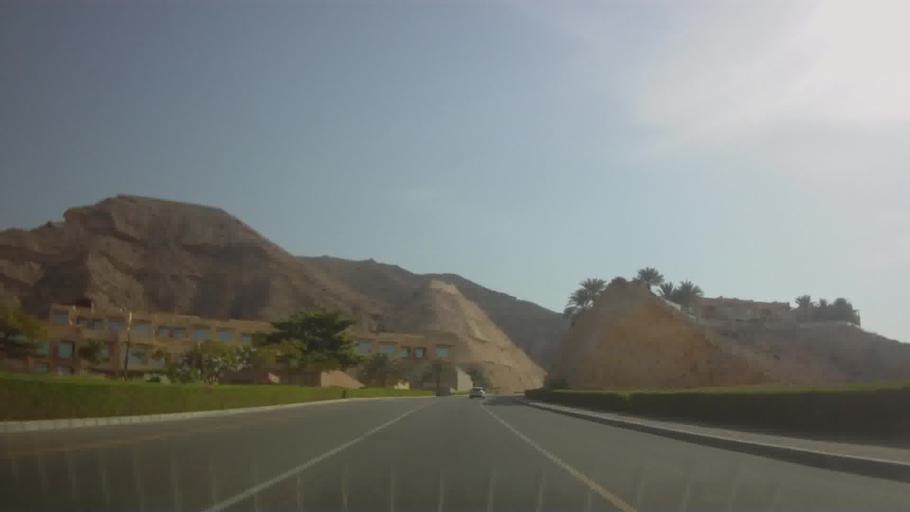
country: OM
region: Muhafazat Masqat
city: Muscat
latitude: 23.5484
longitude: 58.6574
